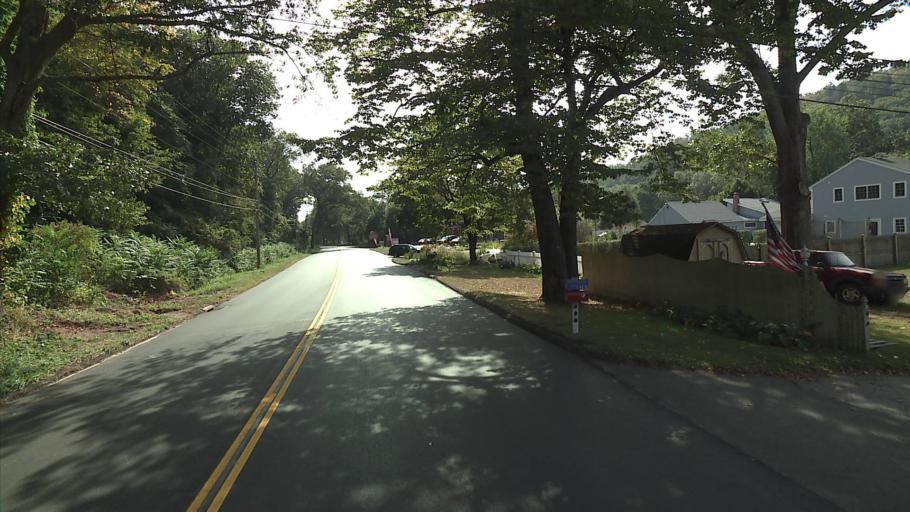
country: US
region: Connecticut
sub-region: Fairfield County
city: Shelton
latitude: 41.3540
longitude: -73.1357
